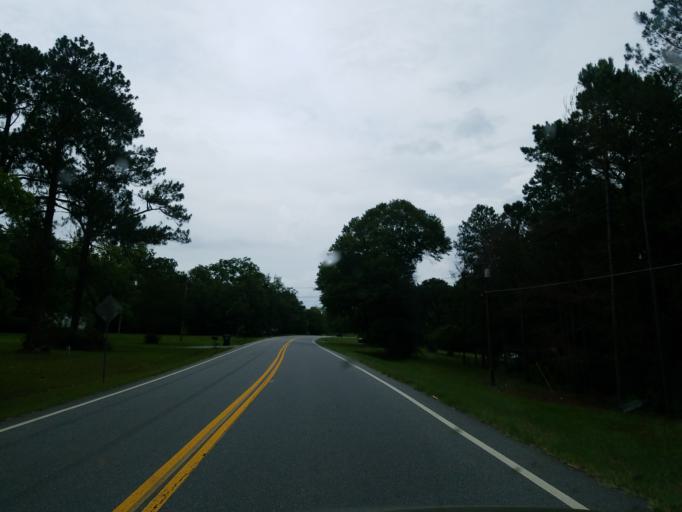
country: US
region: Georgia
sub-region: Crisp County
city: Cordele
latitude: 32.0170
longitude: -83.7313
